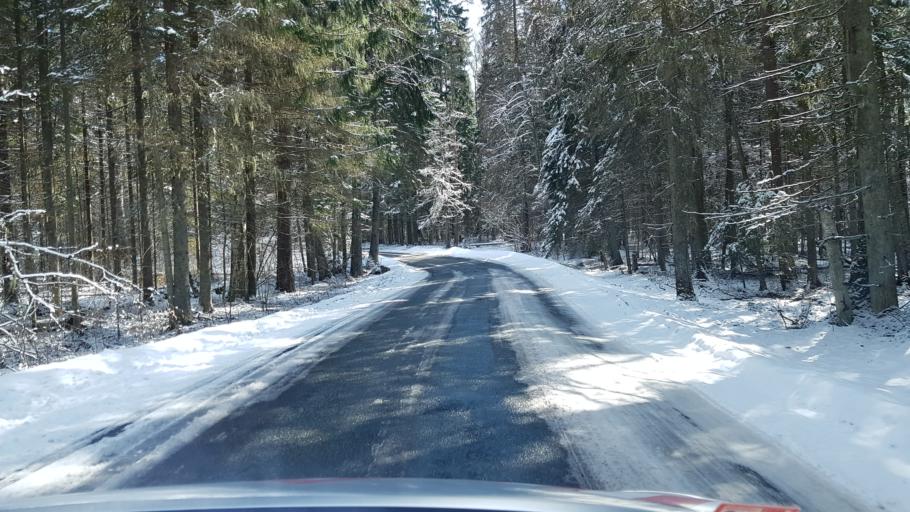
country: EE
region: Laeaene-Virumaa
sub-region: Kadrina vald
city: Kadrina
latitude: 59.5180
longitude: 25.9821
